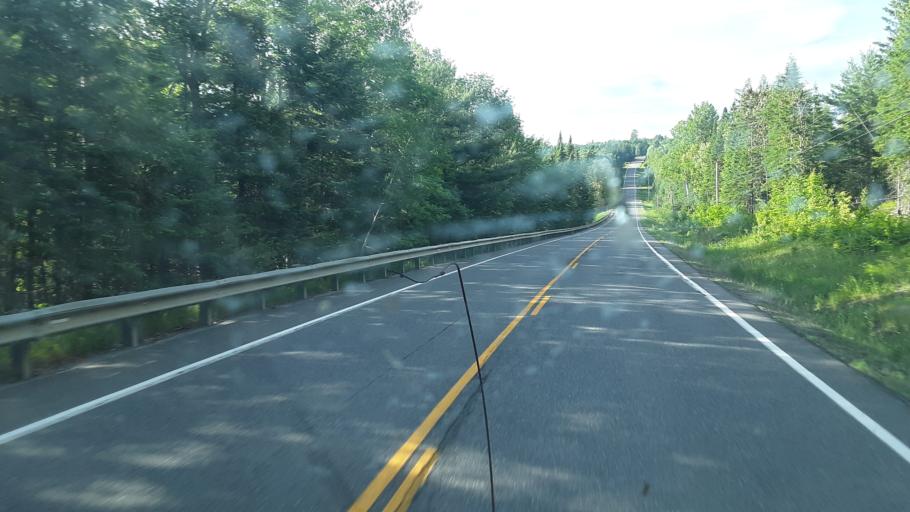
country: US
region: Maine
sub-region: Aroostook County
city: Presque Isle
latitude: 46.4687
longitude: -68.3889
